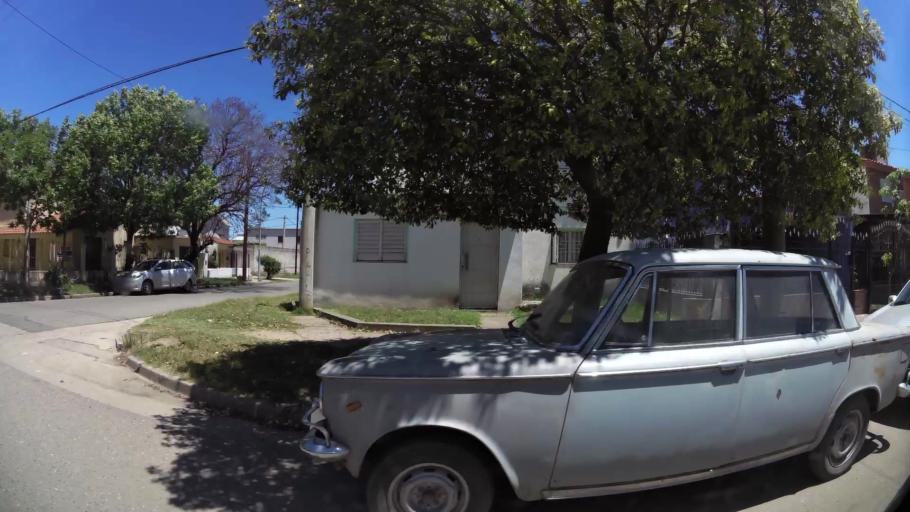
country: AR
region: Cordoba
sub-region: Departamento de Capital
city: Cordoba
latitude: -31.3766
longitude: -64.1331
